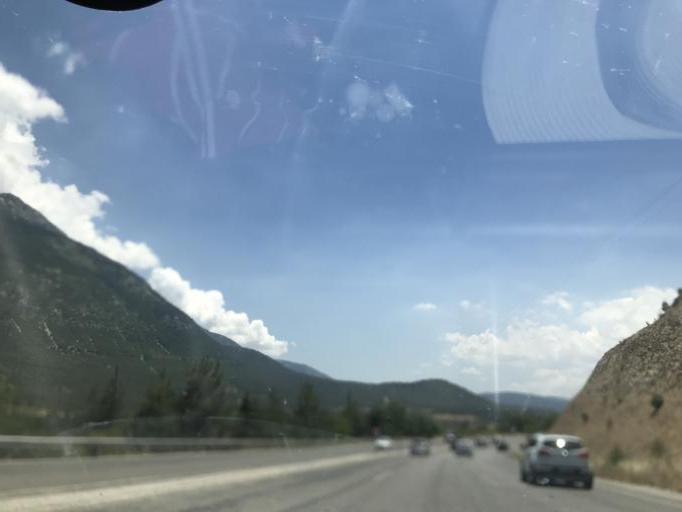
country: TR
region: Denizli
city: Honaz
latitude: 37.7219
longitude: 29.2082
